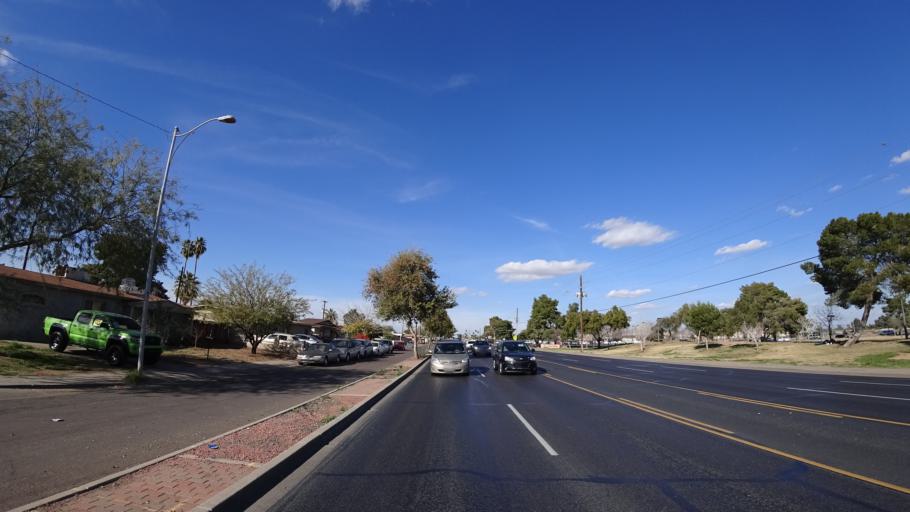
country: US
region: Arizona
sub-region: Maricopa County
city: Tolleson
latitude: 33.4882
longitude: -112.2206
